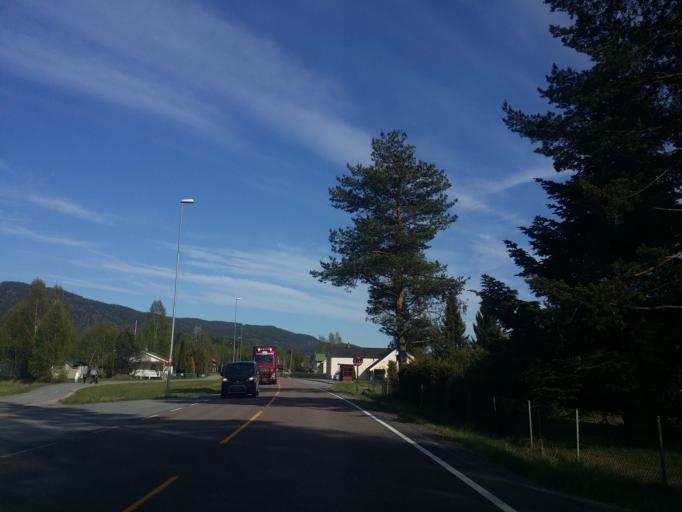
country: NO
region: Telemark
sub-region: Notodden
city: Notodden
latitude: 59.5968
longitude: 9.1341
